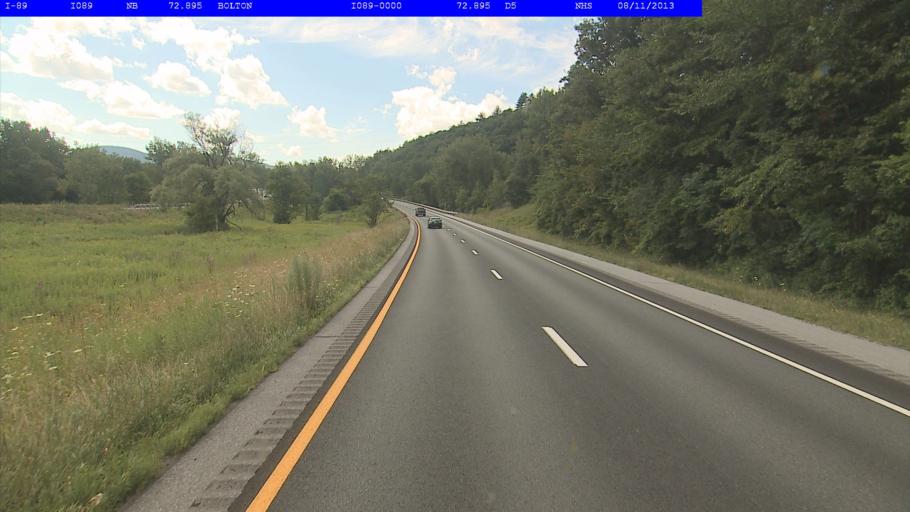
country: US
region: Vermont
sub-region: Chittenden County
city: Jericho
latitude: 44.3827
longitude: -72.9234
